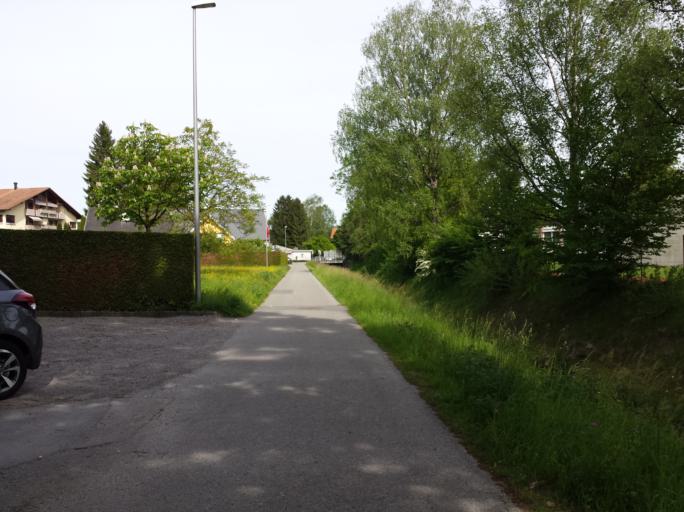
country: CH
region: Saint Gallen
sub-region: Wahlkreis Rheintal
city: Au
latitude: 47.4346
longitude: 9.6334
